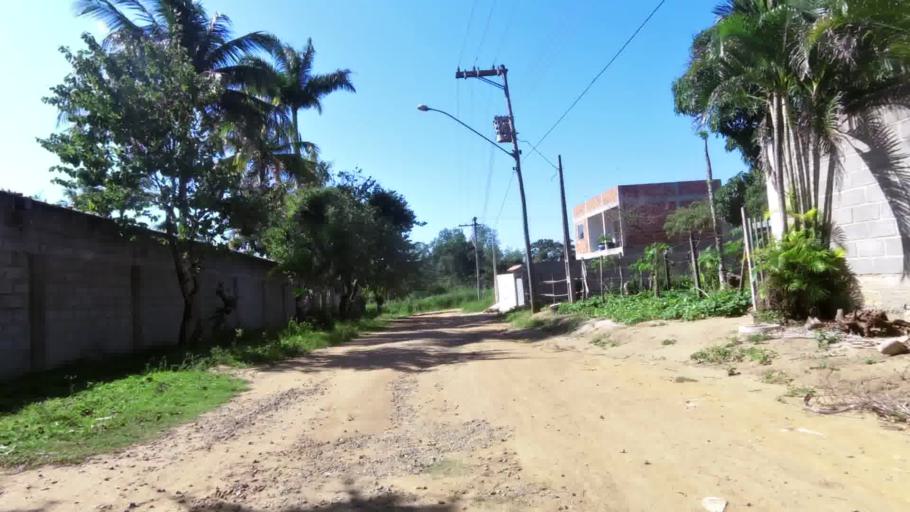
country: BR
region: Espirito Santo
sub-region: Guarapari
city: Guarapari
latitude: -20.7332
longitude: -40.5477
